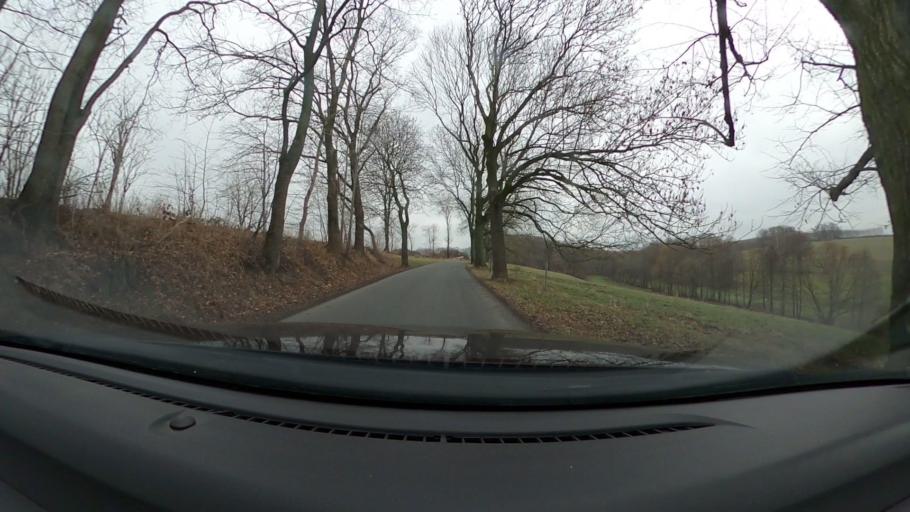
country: DE
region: Saxony
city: Oberschona
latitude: 50.9168
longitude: 13.2530
